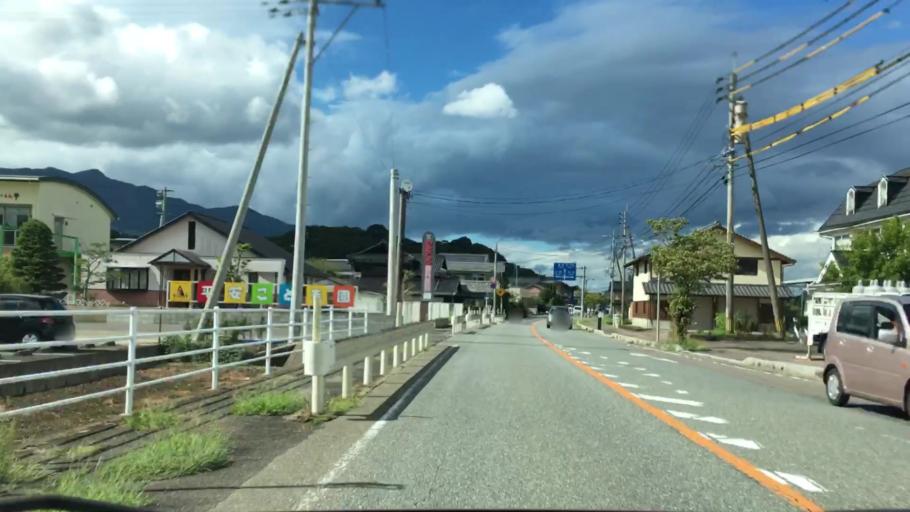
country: JP
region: Saga Prefecture
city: Imaricho-ko
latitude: 33.1935
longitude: 129.8509
